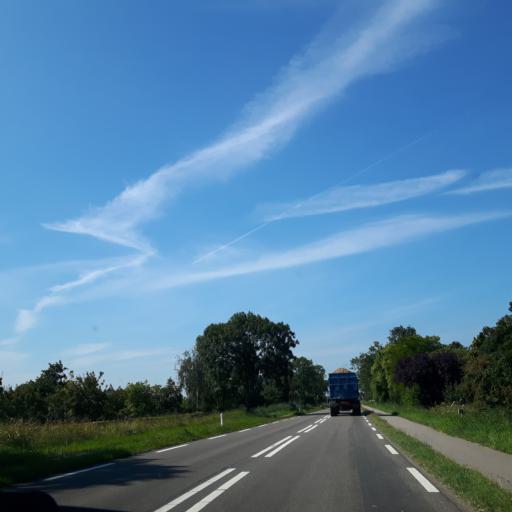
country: NL
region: Zeeland
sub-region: Gemeente Reimerswaal
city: Yerseke
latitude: 51.4284
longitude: 4.1079
